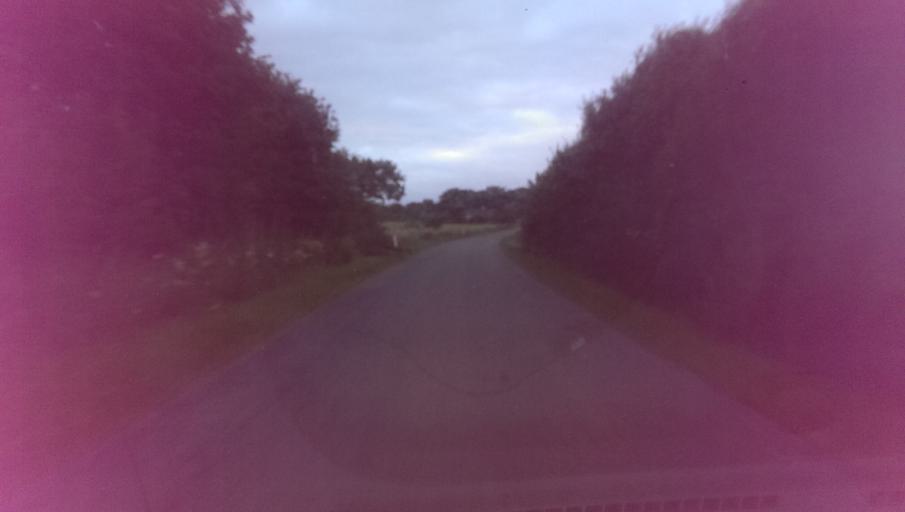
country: DK
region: South Denmark
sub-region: Esbjerg Kommune
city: Tjaereborg
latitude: 55.4881
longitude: 8.5346
